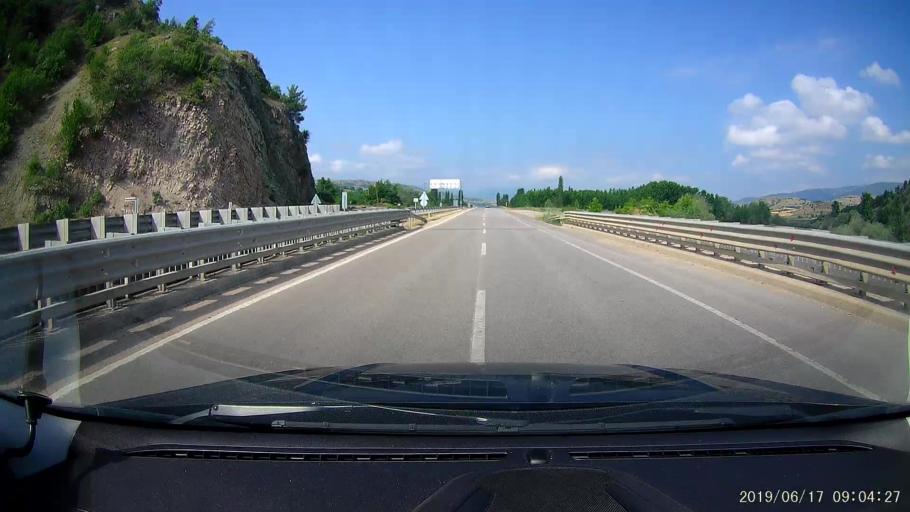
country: TR
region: Amasya
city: Tasova
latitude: 40.7453
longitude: 36.2883
